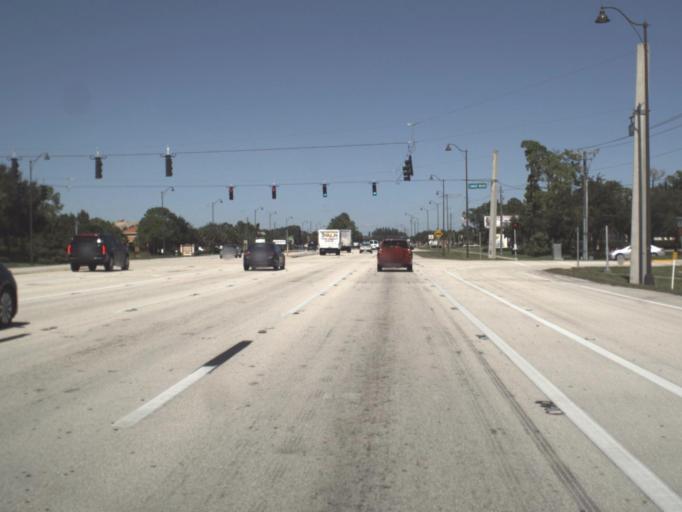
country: US
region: Florida
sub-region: Lee County
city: Bonita Springs
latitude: 26.3735
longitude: -81.8077
